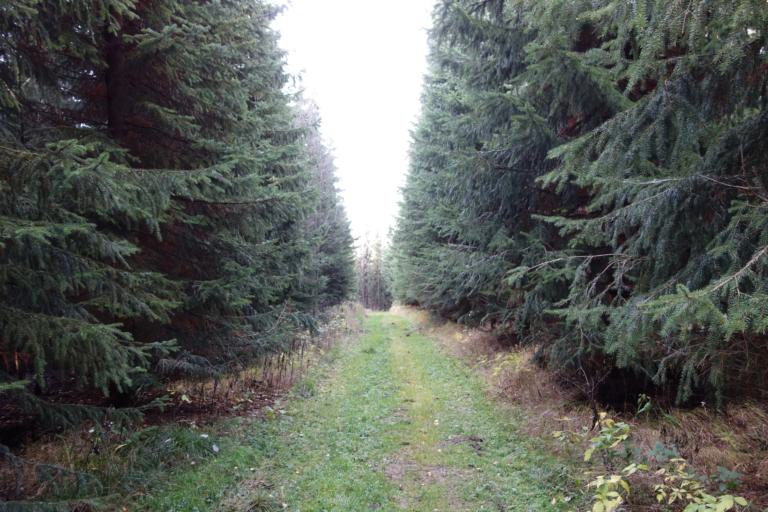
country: DE
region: Saxony
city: Rechenberg-Bienenmuhle
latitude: 50.7193
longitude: 13.5980
